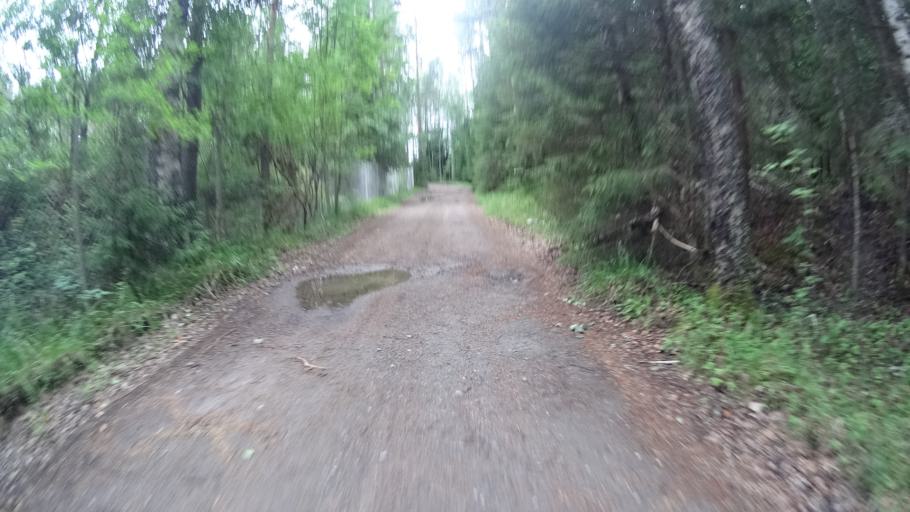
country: FI
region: Uusimaa
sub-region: Helsinki
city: Karkkila
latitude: 60.5975
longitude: 24.1357
